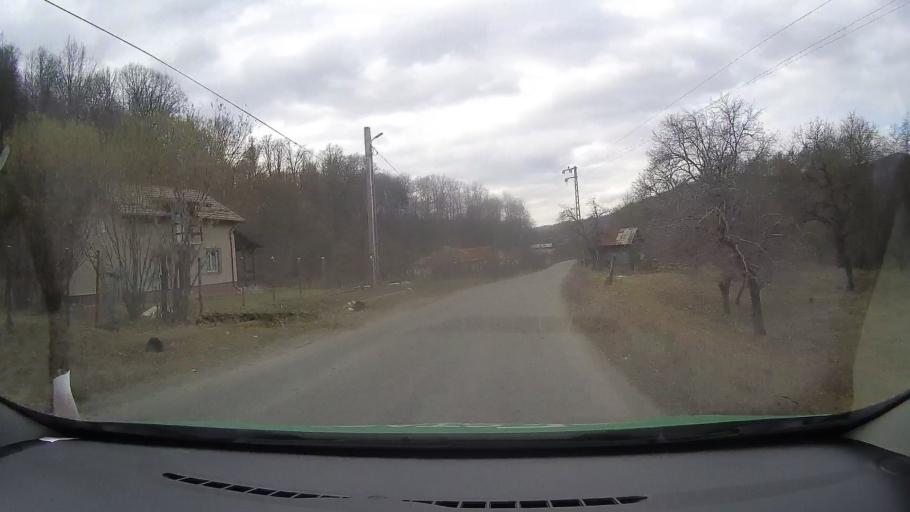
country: RO
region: Dambovita
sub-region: Comuna Valea Lunga
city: Valea Lunga-Cricov
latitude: 45.0836
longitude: 25.5805
